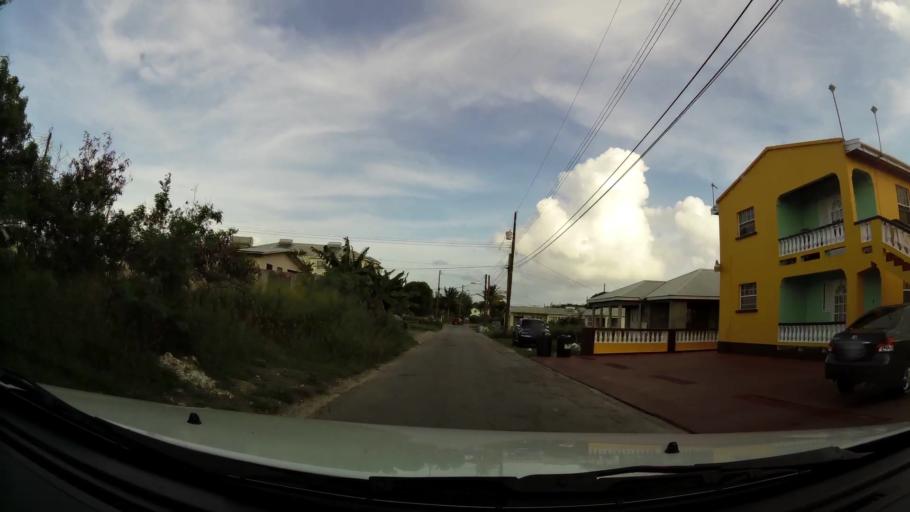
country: BB
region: Christ Church
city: Oistins
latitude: 13.0712
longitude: -59.5395
